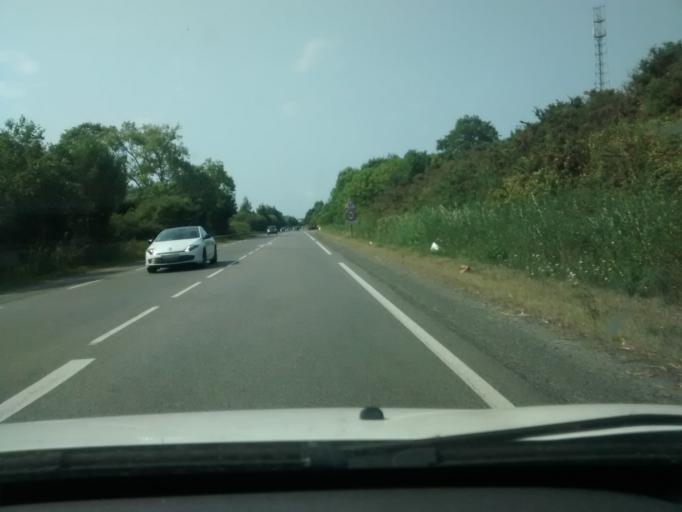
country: FR
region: Pays de la Loire
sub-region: Departement de la Loire-Atlantique
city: Pornichet
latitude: 47.2720
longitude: -2.3267
